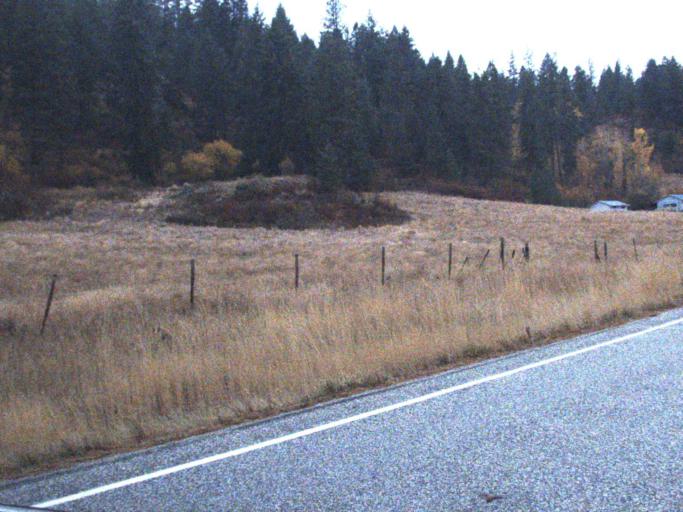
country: US
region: Washington
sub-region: Stevens County
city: Kettle Falls
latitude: 48.7617
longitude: -118.1395
